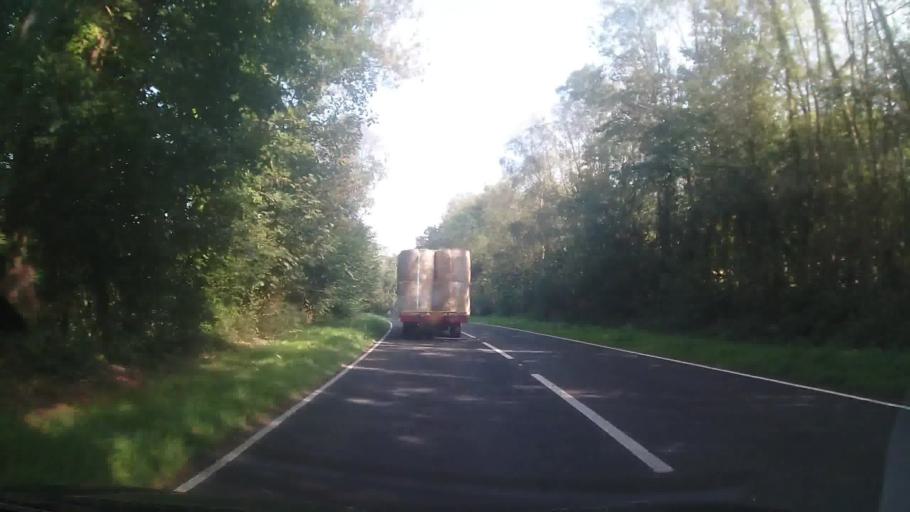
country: GB
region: Wales
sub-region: Pembrokeshire
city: Nevern
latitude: 52.0139
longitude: -4.7761
